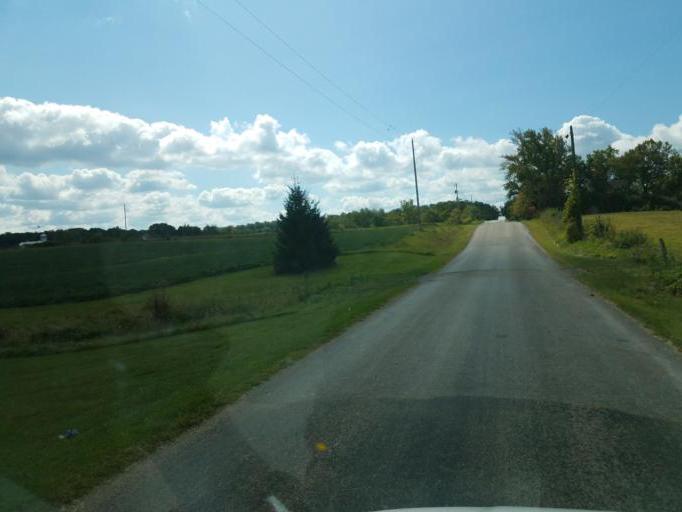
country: US
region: Ohio
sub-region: Wayne County
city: West Salem
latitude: 41.0428
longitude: -82.0963
